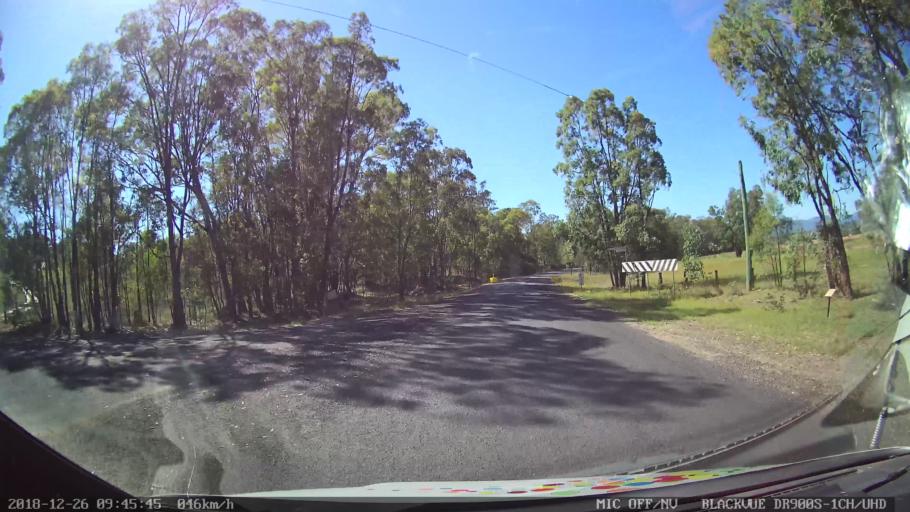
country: AU
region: New South Wales
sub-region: Mid-Western Regional
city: Kandos
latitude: -32.9637
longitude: 150.1056
